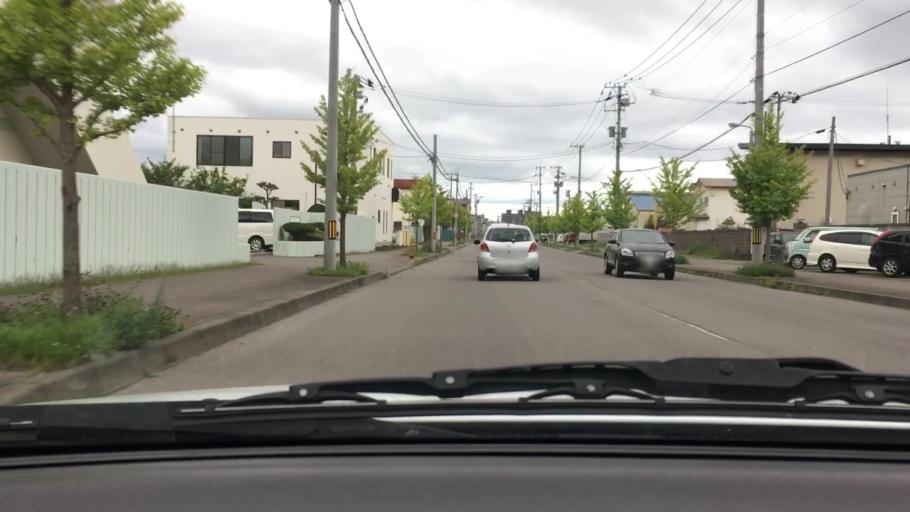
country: JP
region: Hokkaido
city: Hakodate
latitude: 41.7924
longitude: 140.7279
